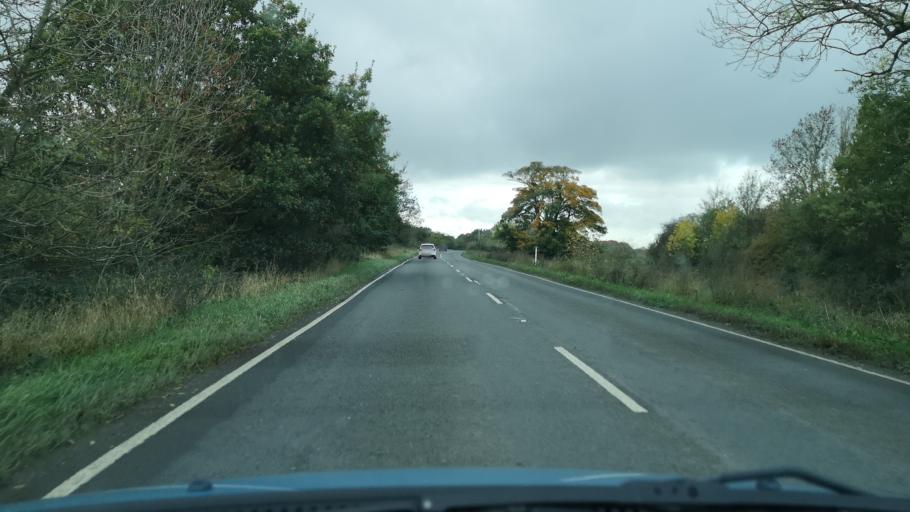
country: GB
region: England
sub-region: North Lincolnshire
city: Belton
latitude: 53.5828
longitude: -0.8076
